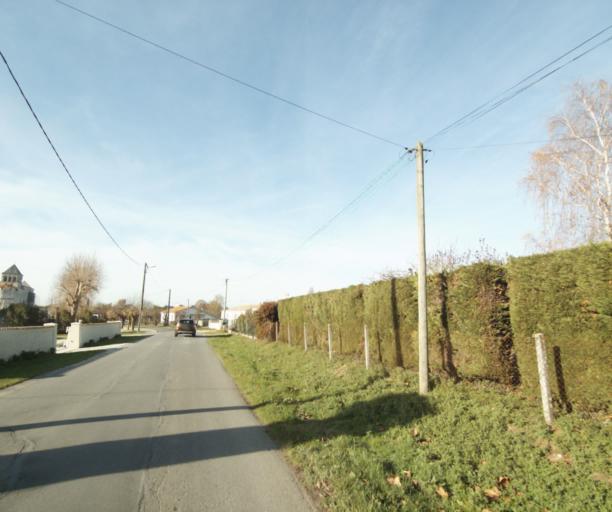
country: FR
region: Poitou-Charentes
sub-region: Departement de la Charente-Maritime
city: Chaniers
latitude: 45.7162
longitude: -0.5546
